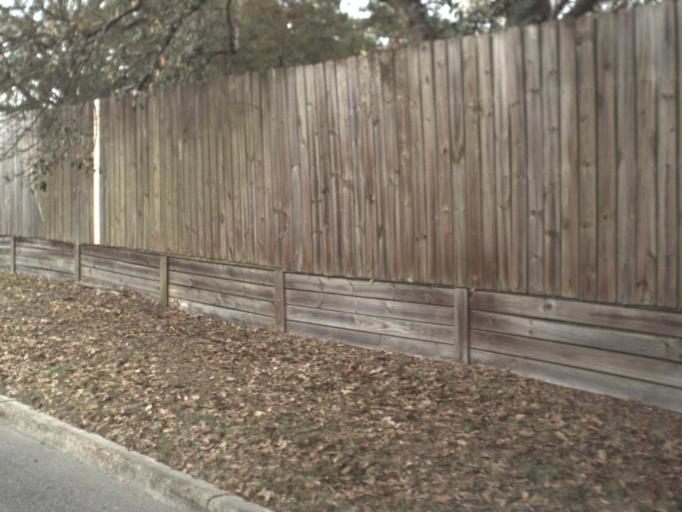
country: US
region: Florida
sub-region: Bay County
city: Springfield
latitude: 30.1558
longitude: -85.6251
